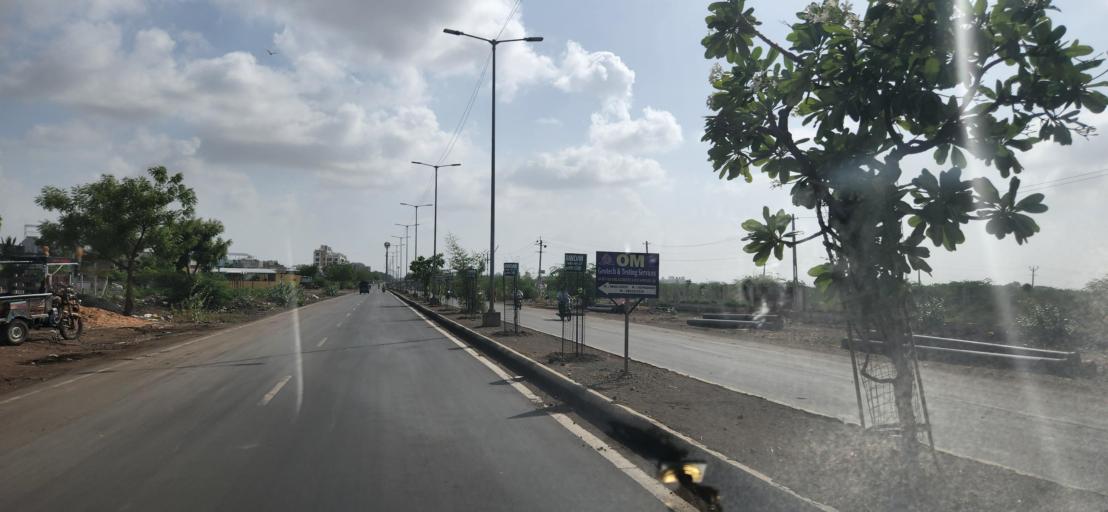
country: IN
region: Gujarat
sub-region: Bhavnagar
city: Bhavnagar
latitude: 21.7370
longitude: 72.1595
